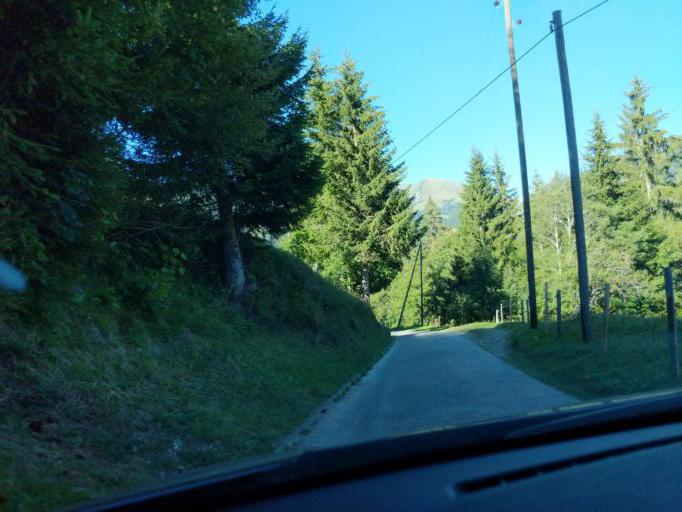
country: CH
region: Fribourg
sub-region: Gruyere District
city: Charmey
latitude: 46.5986
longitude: 7.2695
